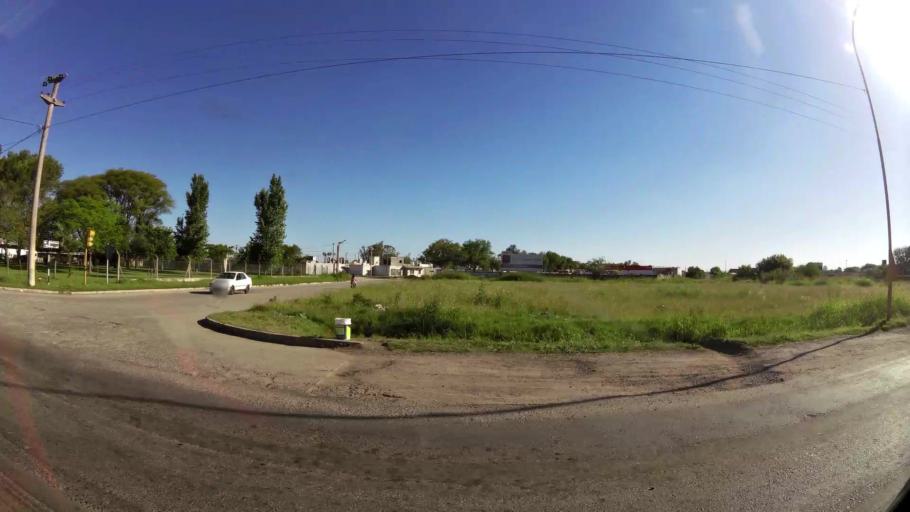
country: AR
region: Cordoba
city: San Francisco
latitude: -31.4197
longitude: -62.0652
